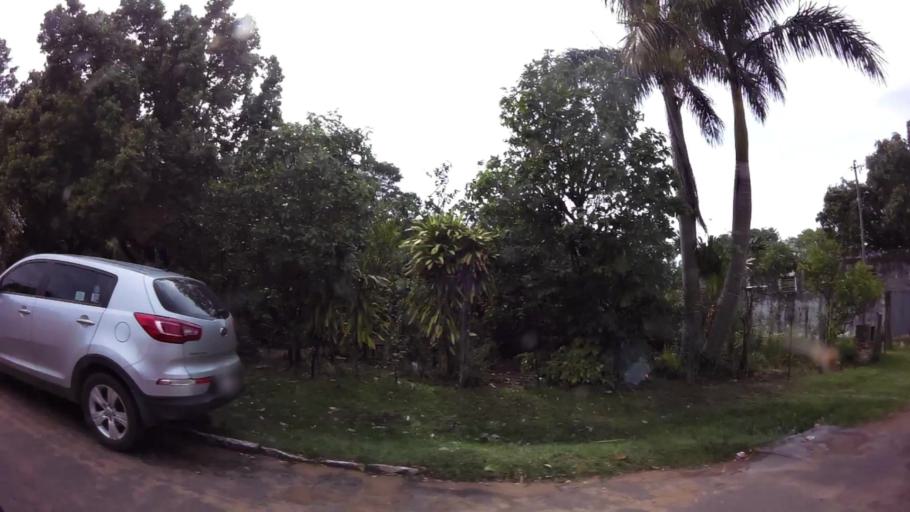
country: PY
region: Central
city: Limpio
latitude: -25.1414
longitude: -57.4725
